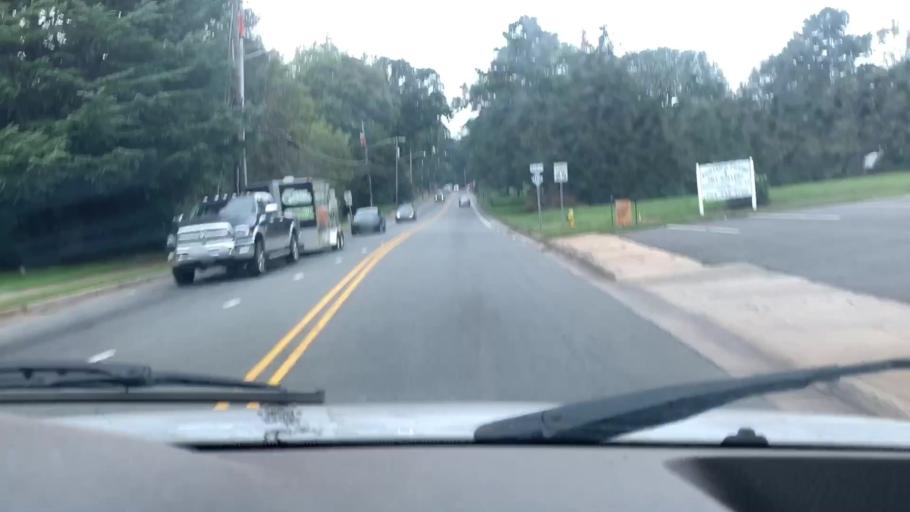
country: US
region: North Carolina
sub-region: Mecklenburg County
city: Huntersville
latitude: 35.4113
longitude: -80.8430
